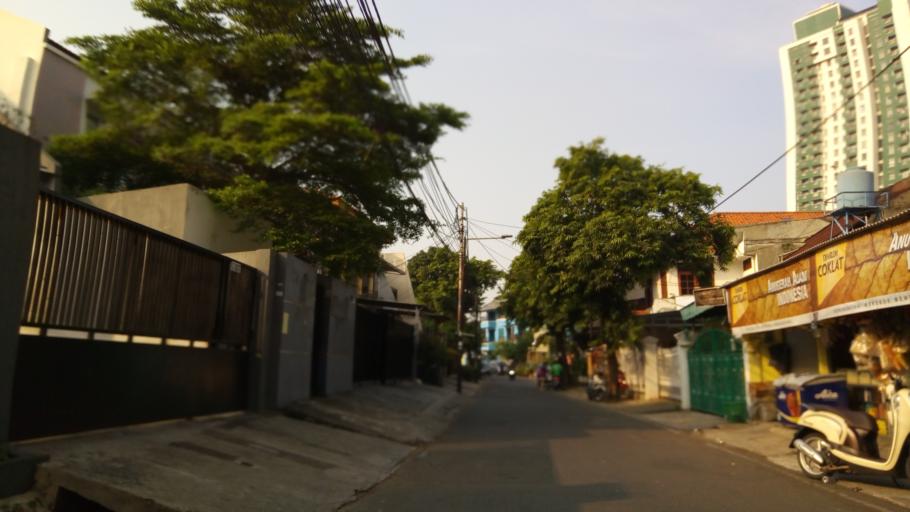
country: ID
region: Jakarta Raya
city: Jakarta
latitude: -6.1952
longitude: 106.8540
